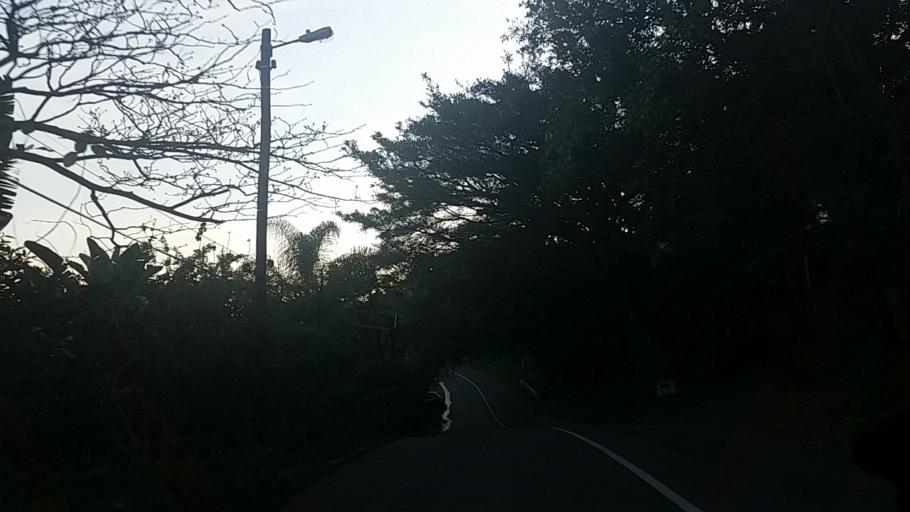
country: ZA
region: KwaZulu-Natal
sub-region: eThekwini Metropolitan Municipality
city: Berea
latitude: -29.8504
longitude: 30.9169
